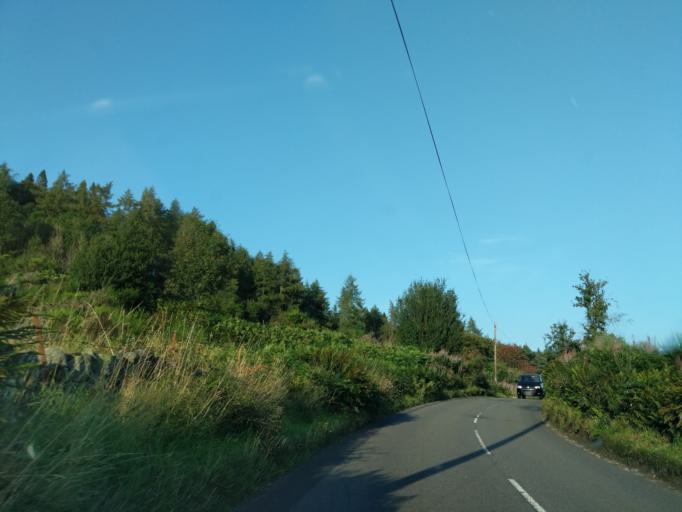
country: GB
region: Scotland
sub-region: Stirling
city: Balfron
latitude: 56.1755
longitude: -4.3545
